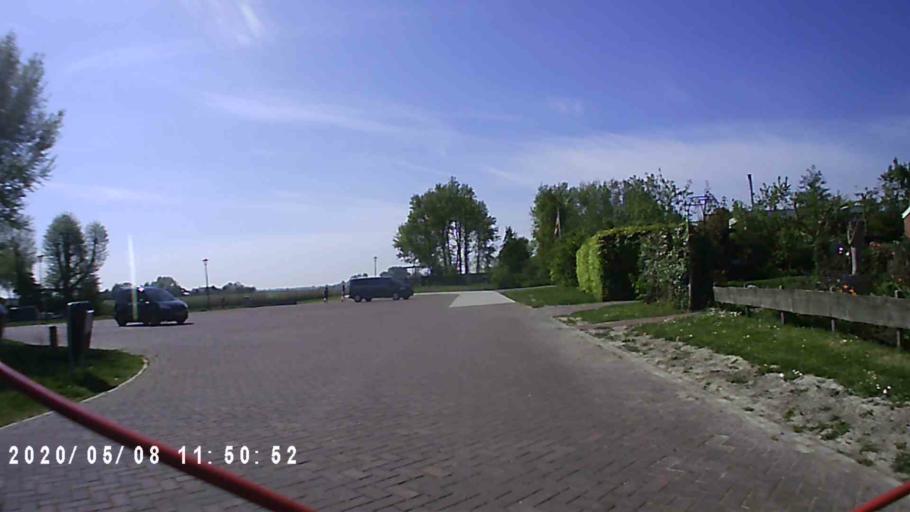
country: NL
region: Groningen
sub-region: Gemeente Bedum
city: Bedum
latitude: 53.3203
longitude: 6.6946
